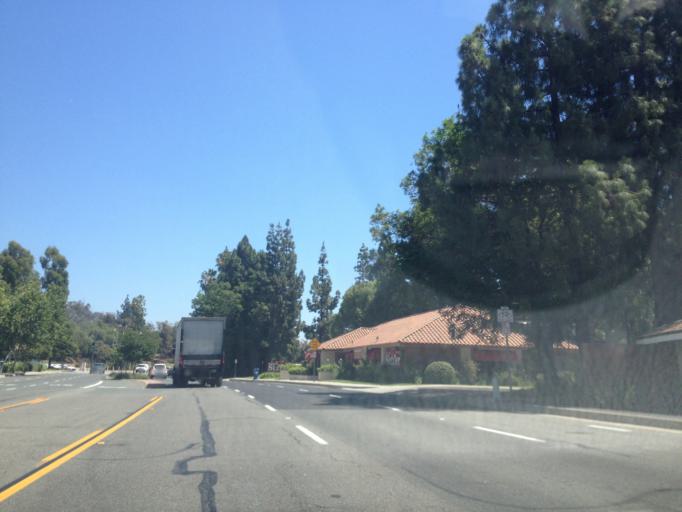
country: US
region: California
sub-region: Orange County
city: Fullerton
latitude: 33.8844
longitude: -117.9258
